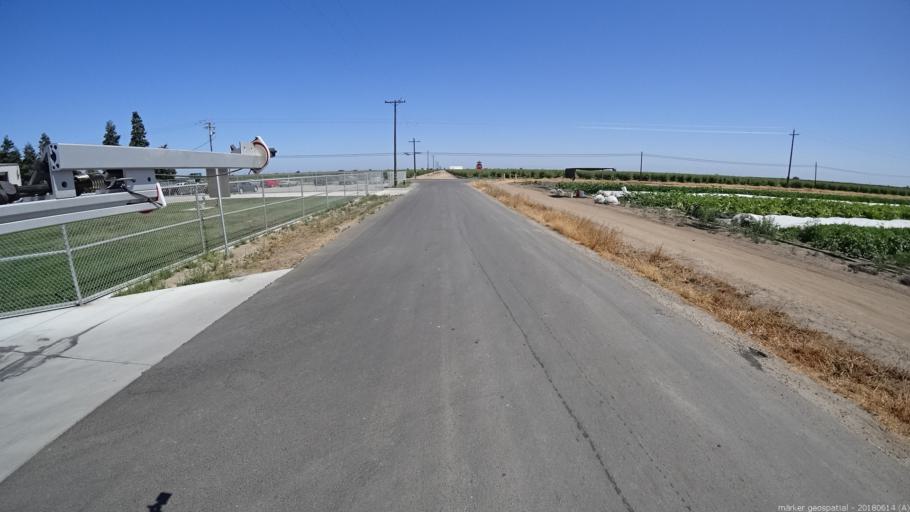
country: US
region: California
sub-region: Madera County
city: Fairmead
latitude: 36.9520
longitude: -120.1930
